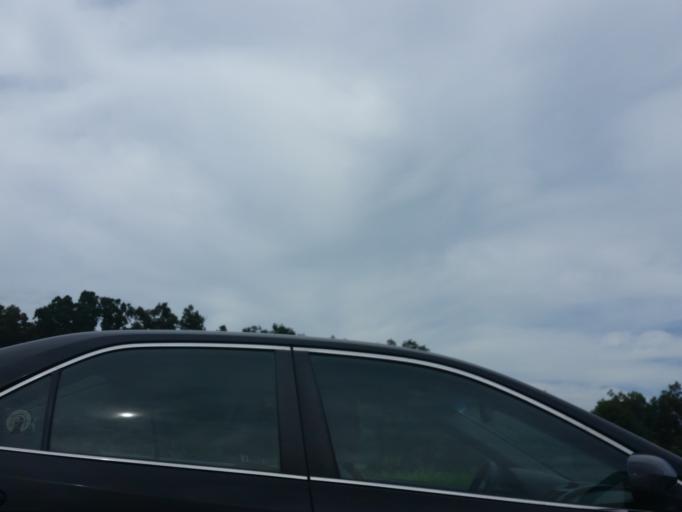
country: US
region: Kentucky
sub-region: Trigg County
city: Cadiz
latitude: 36.9583
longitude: -87.8541
